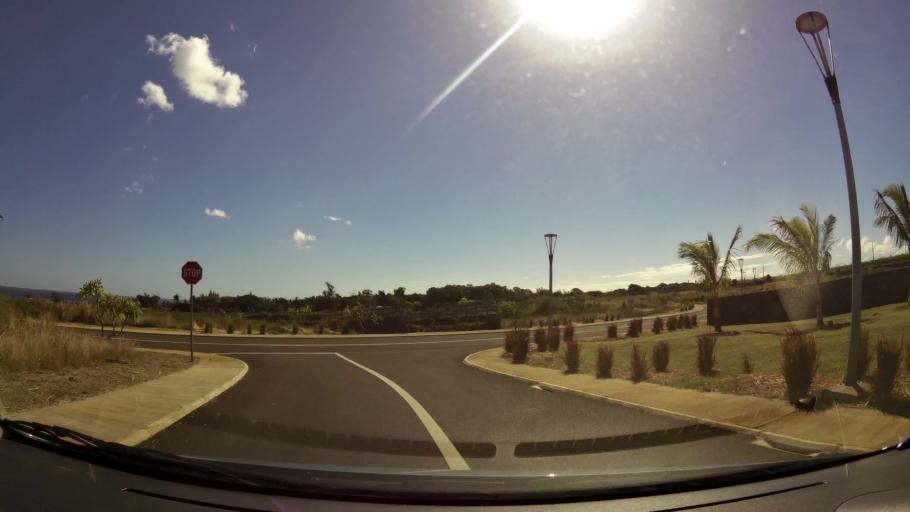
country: MU
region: Black River
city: Flic en Flac
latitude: -20.2705
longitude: 57.3859
